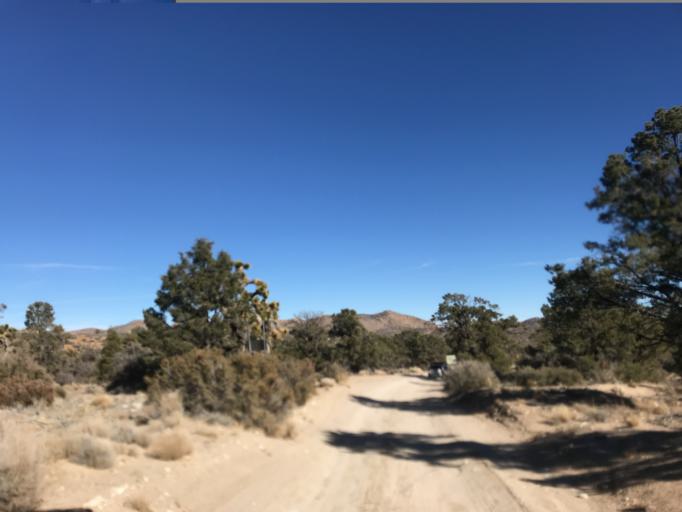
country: US
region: California
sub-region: San Bernardino County
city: Big Bear City
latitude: 34.2342
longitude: -116.6485
